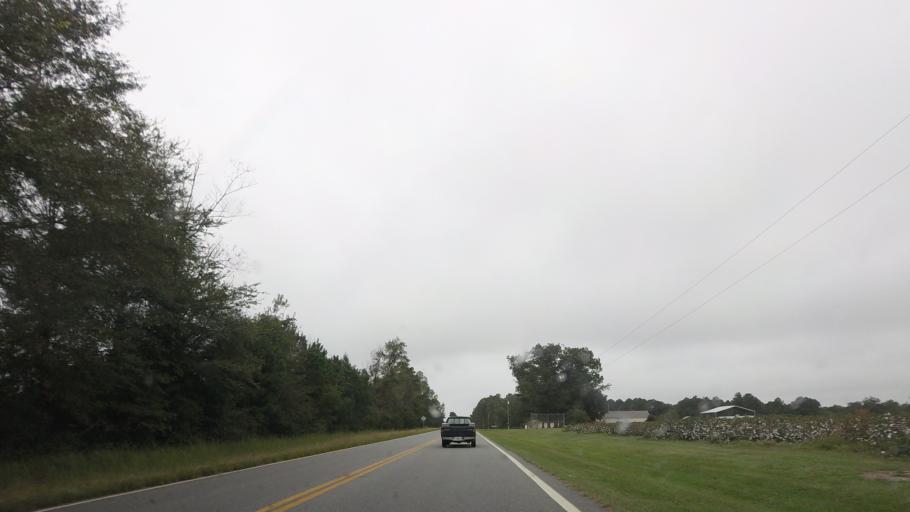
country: US
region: Georgia
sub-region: Berrien County
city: Enigma
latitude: 31.4210
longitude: -83.2448
